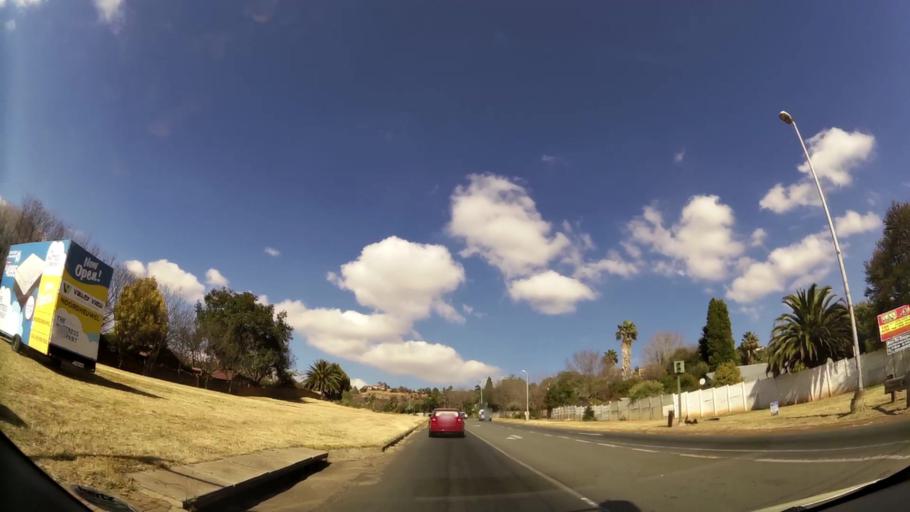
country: ZA
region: Gauteng
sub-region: City of Johannesburg Metropolitan Municipality
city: Roodepoort
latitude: -26.1086
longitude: 27.8386
